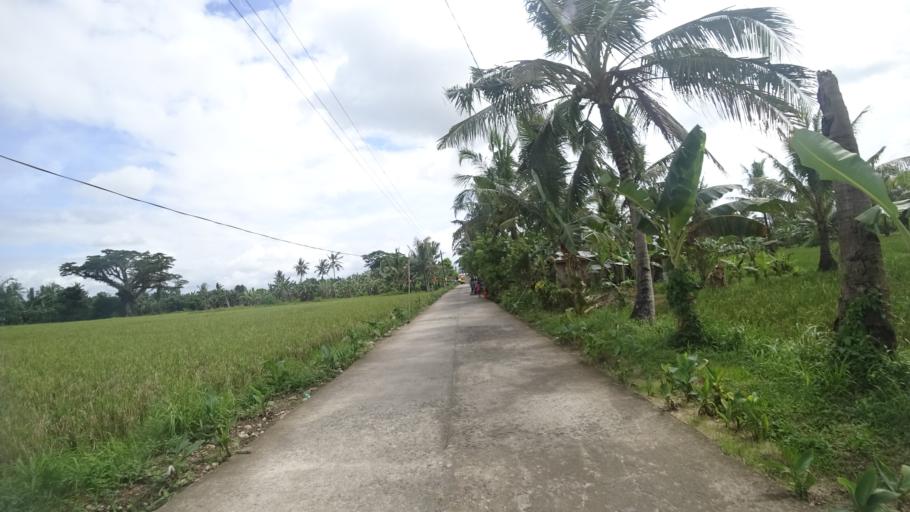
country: PH
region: Eastern Visayas
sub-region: Province of Leyte
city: Santa Fe
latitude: 11.1705
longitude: 124.8864
